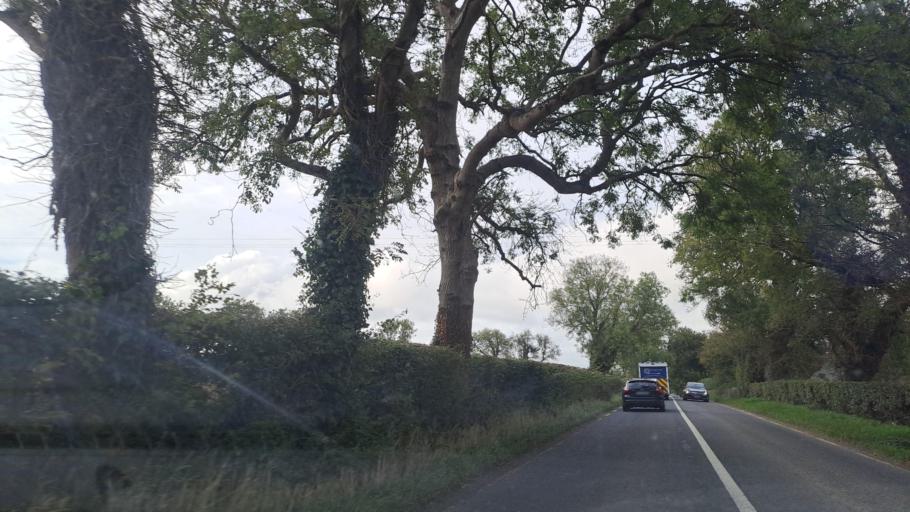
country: IE
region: Leinster
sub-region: An Mhi
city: Navan
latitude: 53.7168
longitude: -6.6963
